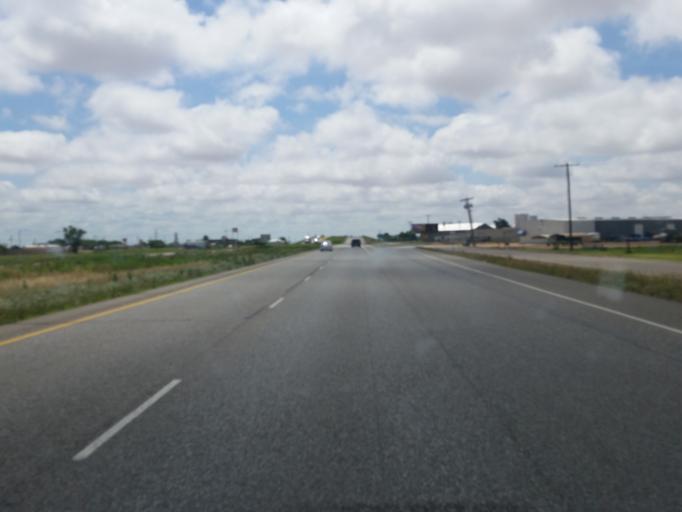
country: US
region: Texas
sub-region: Lubbock County
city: Slaton
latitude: 33.4232
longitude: -101.6486
